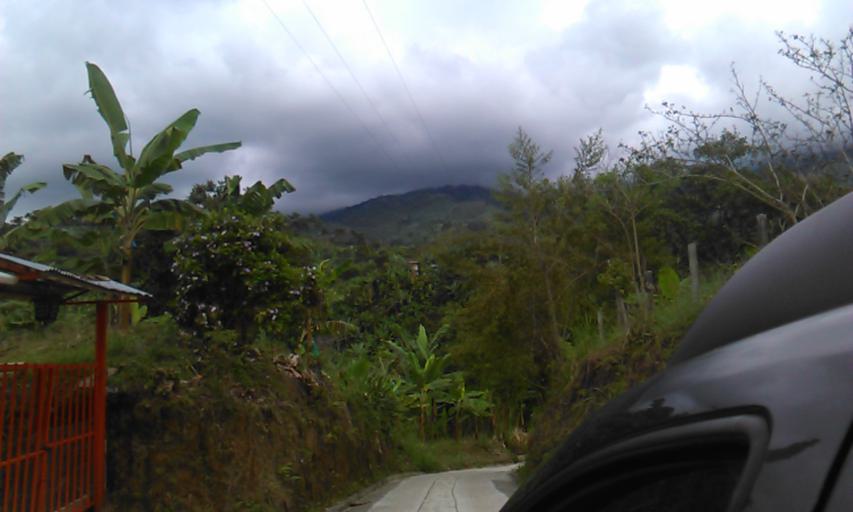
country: CO
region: Quindio
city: Cordoba
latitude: 4.4122
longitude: -75.6824
